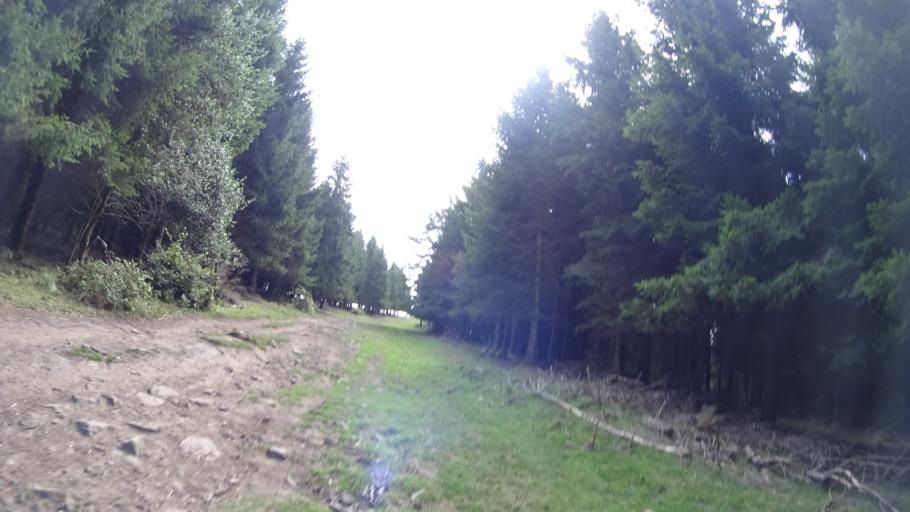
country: ES
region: Basque Country
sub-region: Bizkaia
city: Manaria
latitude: 43.0978
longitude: -2.6359
